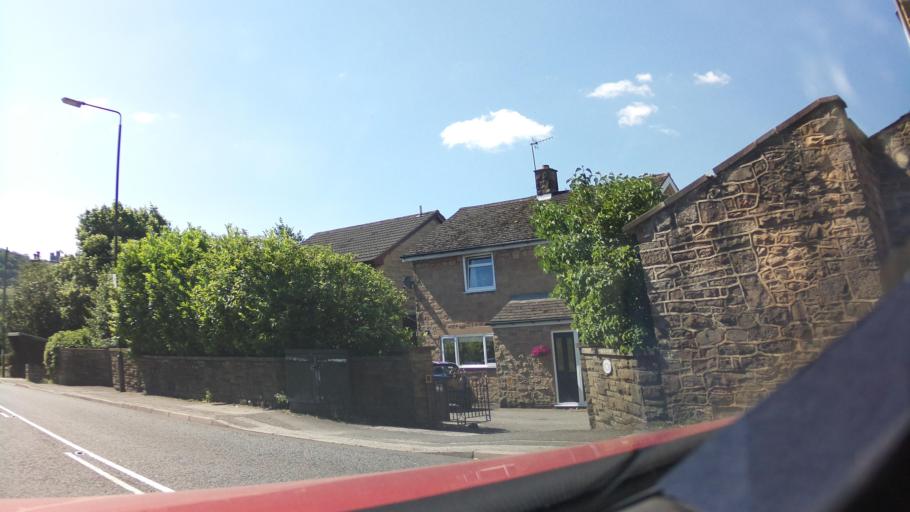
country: GB
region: England
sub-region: Derbyshire
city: Matlock
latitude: 53.1386
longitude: -1.5480
